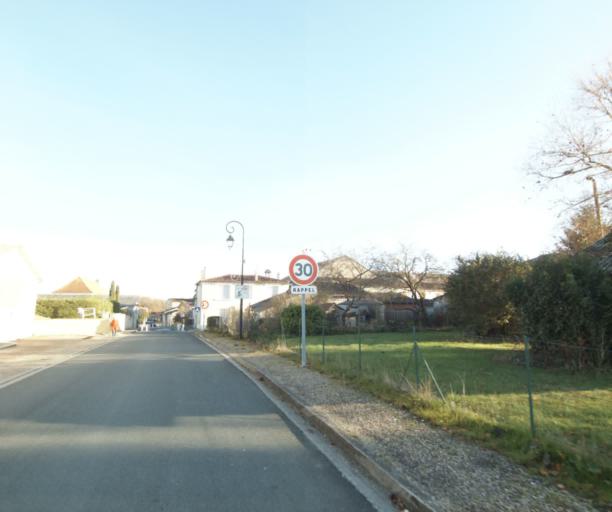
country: FR
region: Poitou-Charentes
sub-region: Departement de la Charente-Maritime
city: Cherac
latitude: 45.7029
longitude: -0.4398
